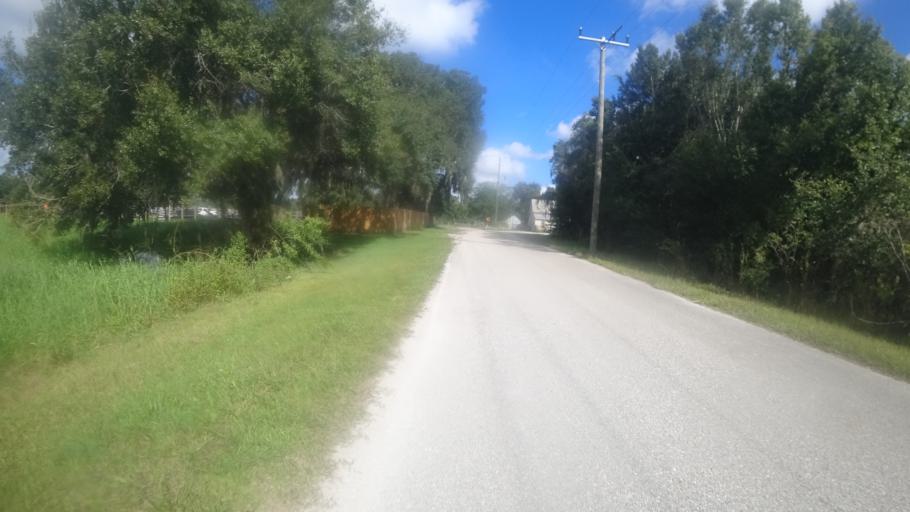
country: US
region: Florida
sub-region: Manatee County
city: Samoset
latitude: 27.4720
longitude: -82.4588
